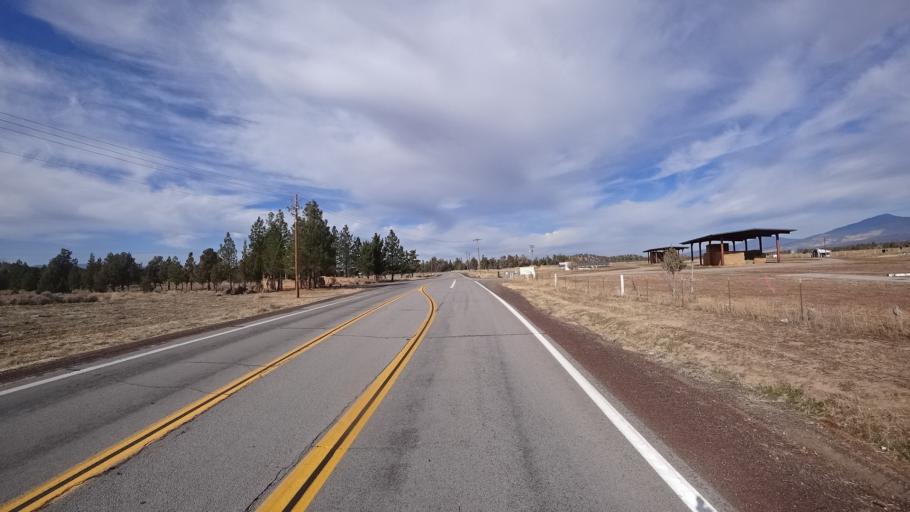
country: US
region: California
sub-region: Siskiyou County
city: Weed
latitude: 41.5509
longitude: -122.3802
